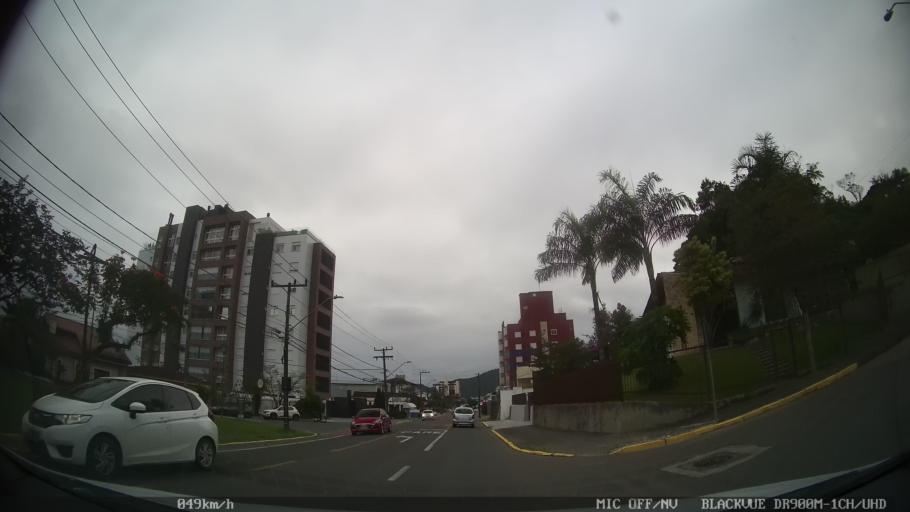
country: BR
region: Santa Catarina
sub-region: Joinville
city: Joinville
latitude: -26.2844
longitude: -48.8529
